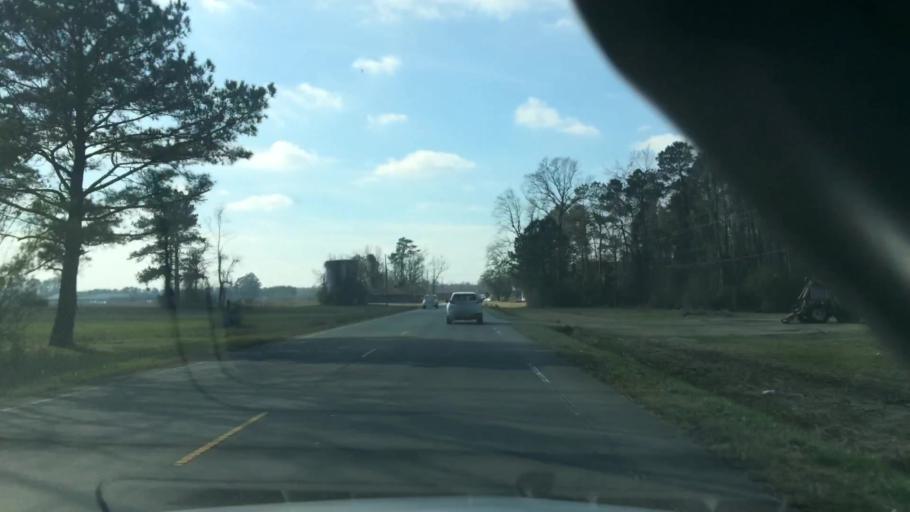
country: US
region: North Carolina
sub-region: Duplin County
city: Beulaville
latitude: 34.8316
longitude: -77.8056
